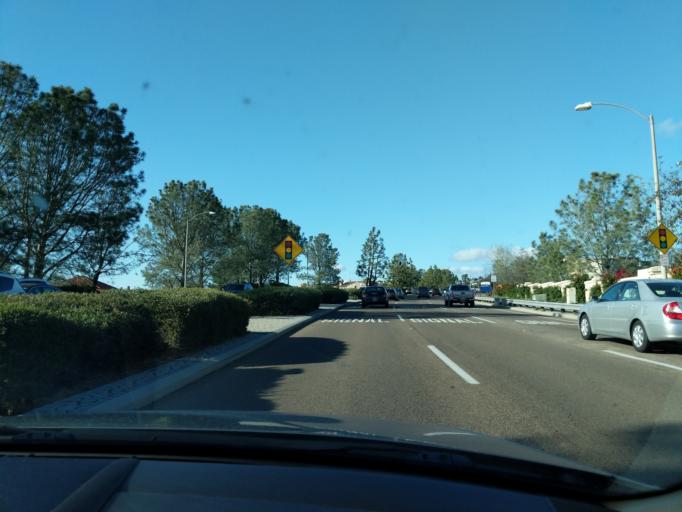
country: US
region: California
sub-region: San Diego County
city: Lake San Marcos
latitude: 33.0790
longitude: -117.2386
